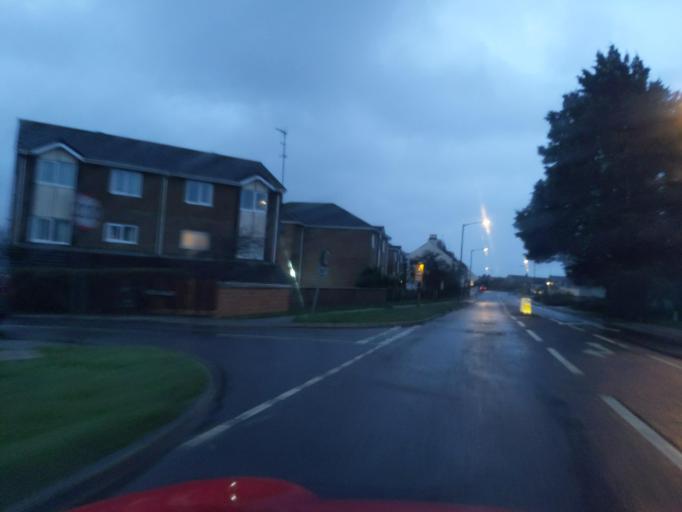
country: GB
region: England
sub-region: Cornwall
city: Torpoint
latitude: 50.3781
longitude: -4.2054
